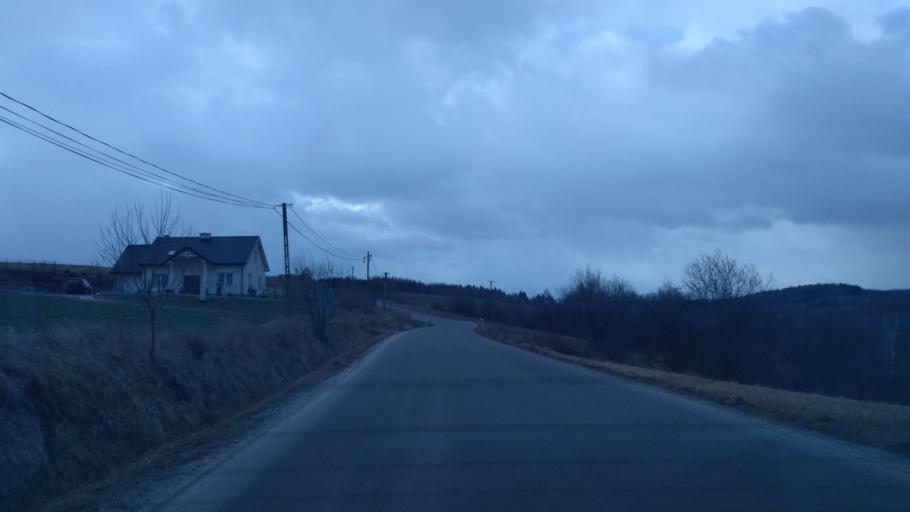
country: PL
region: Subcarpathian Voivodeship
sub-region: Powiat rzeszowski
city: Blazowa
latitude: 49.8699
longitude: 22.0992
